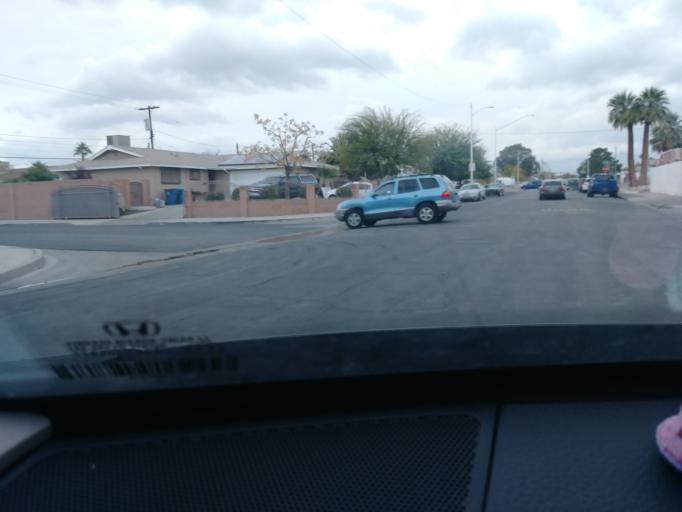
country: US
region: Nevada
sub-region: Clark County
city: Spring Valley
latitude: 36.1632
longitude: -115.2227
